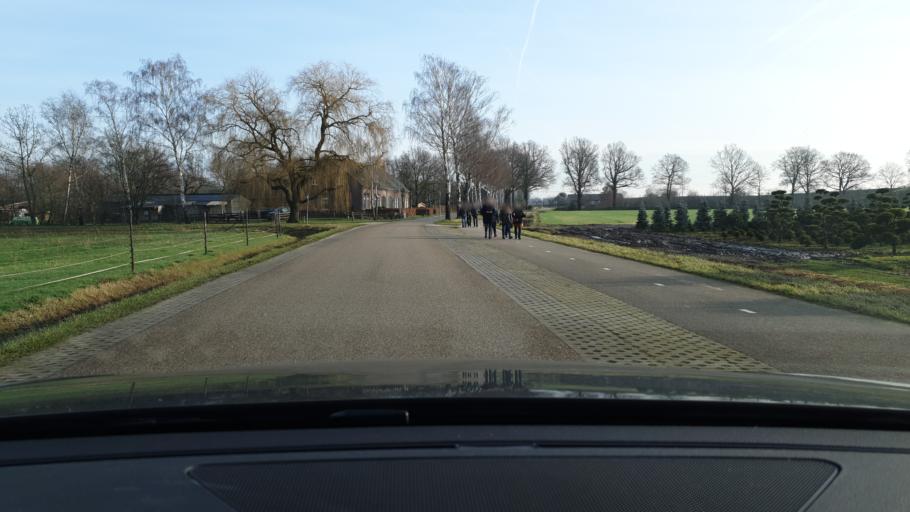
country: NL
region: Limburg
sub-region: Gemeente Peel en Maas
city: Maasbree
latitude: 51.4405
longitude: 6.0875
